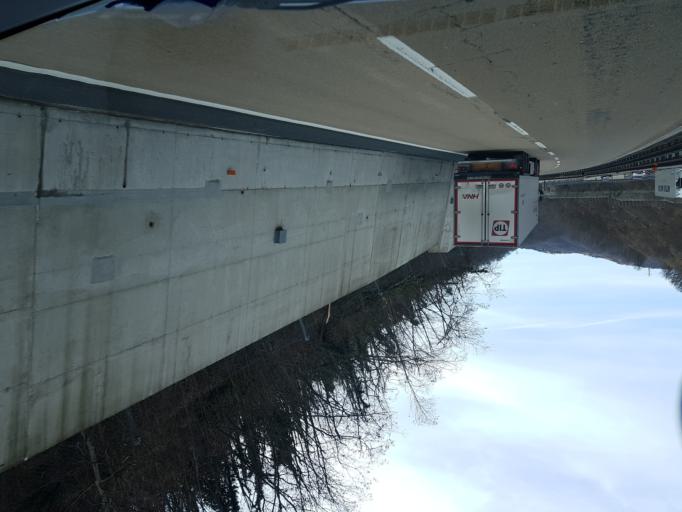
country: IT
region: Liguria
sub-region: Provincia di Genova
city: Isola del Cantone
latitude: 44.6333
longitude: 8.9457
